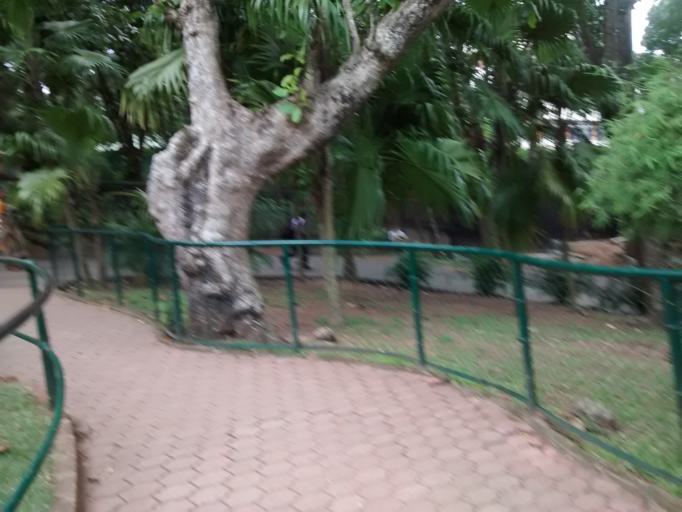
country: IN
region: Kerala
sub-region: Thiruvananthapuram
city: Thiruvananthapuram
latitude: 8.5095
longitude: 76.9536
